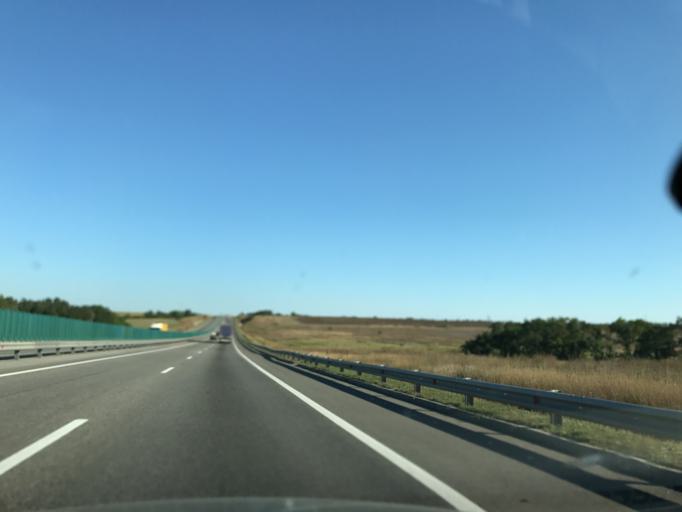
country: RU
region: Rostov
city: Glubokiy
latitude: 48.6030
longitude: 40.3541
